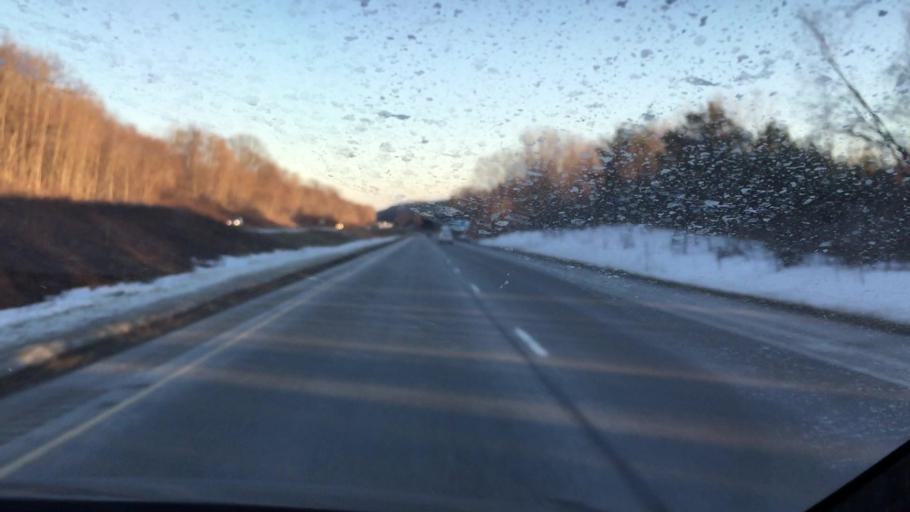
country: US
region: Pennsylvania
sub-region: Crawford County
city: Meadville
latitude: 41.6361
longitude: -80.1960
